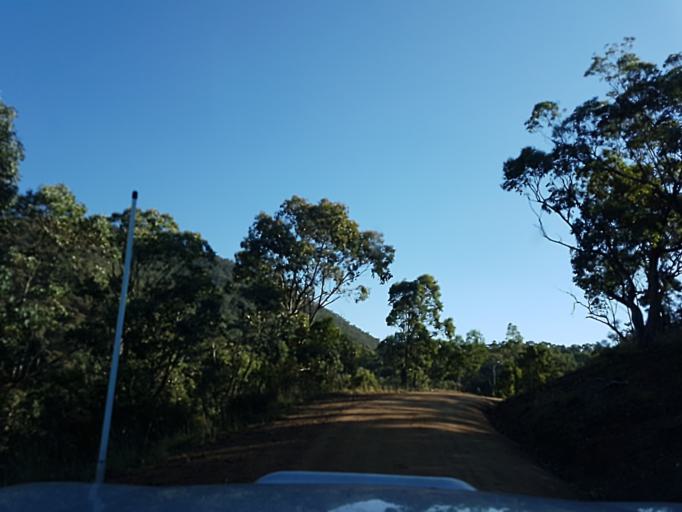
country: AU
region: New South Wales
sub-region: Snowy River
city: Jindabyne
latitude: -36.9368
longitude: 148.3385
